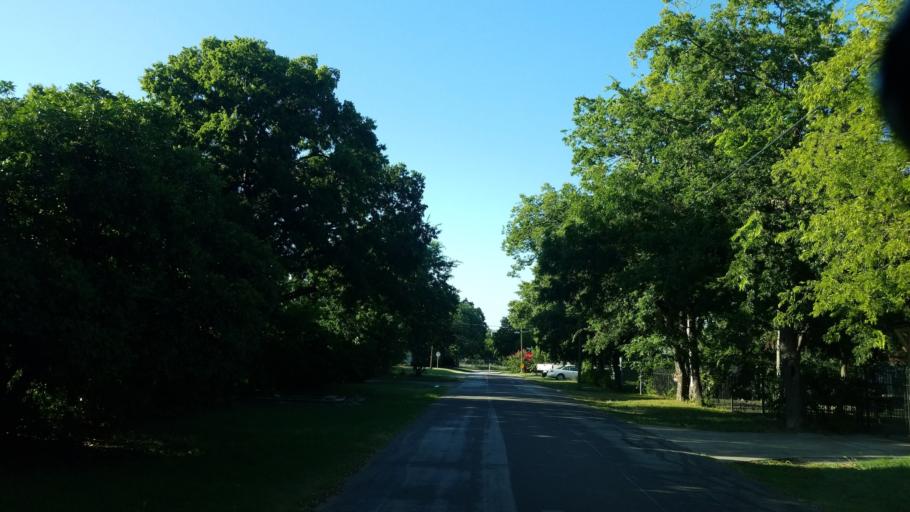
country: US
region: Texas
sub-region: Dallas County
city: Balch Springs
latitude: 32.7757
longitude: -96.7045
